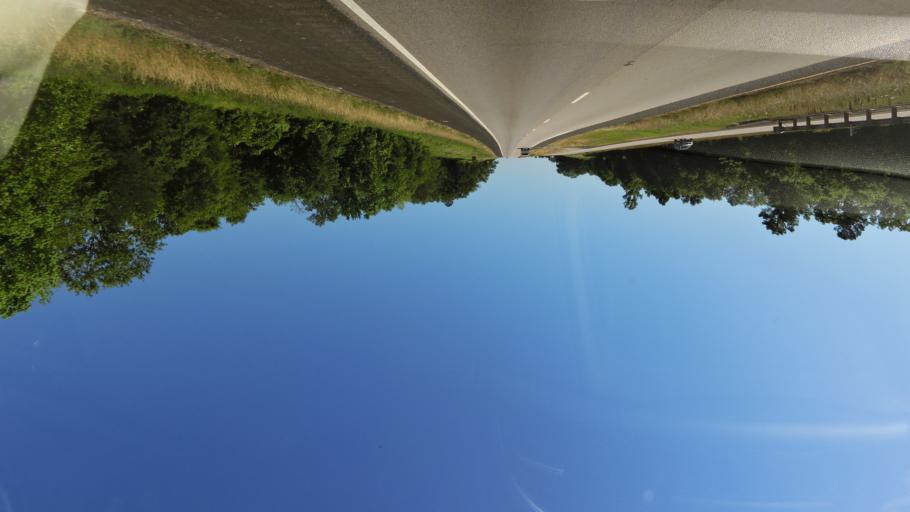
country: US
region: Texas
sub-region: Angelina County
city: Redland
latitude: 31.4476
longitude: -94.7267
